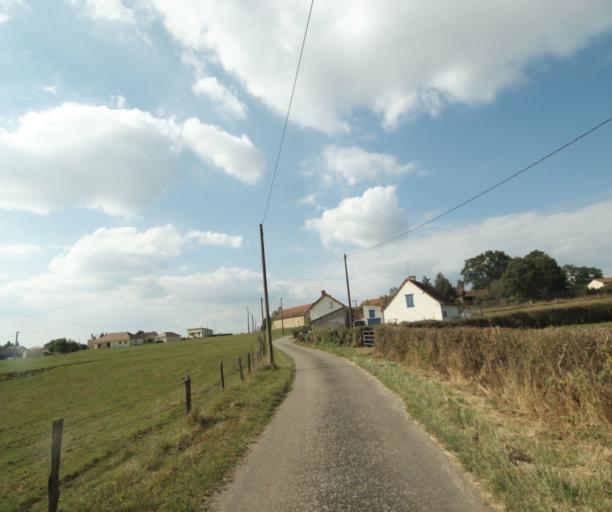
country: FR
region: Bourgogne
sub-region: Departement de Saone-et-Loire
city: Palinges
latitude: 46.4952
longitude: 4.2196
